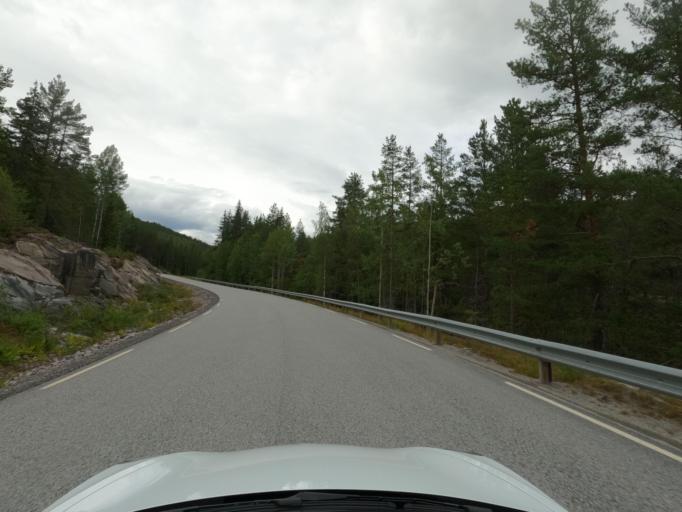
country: NO
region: Telemark
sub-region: Notodden
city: Notodden
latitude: 59.6996
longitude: 9.1329
